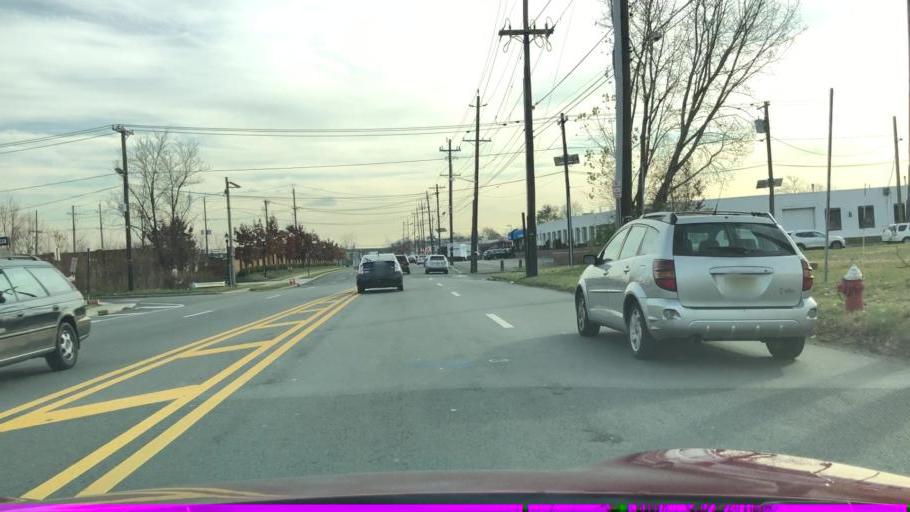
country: US
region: New Jersey
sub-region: Bergen County
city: Bogota
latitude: 40.8731
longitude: -74.0400
